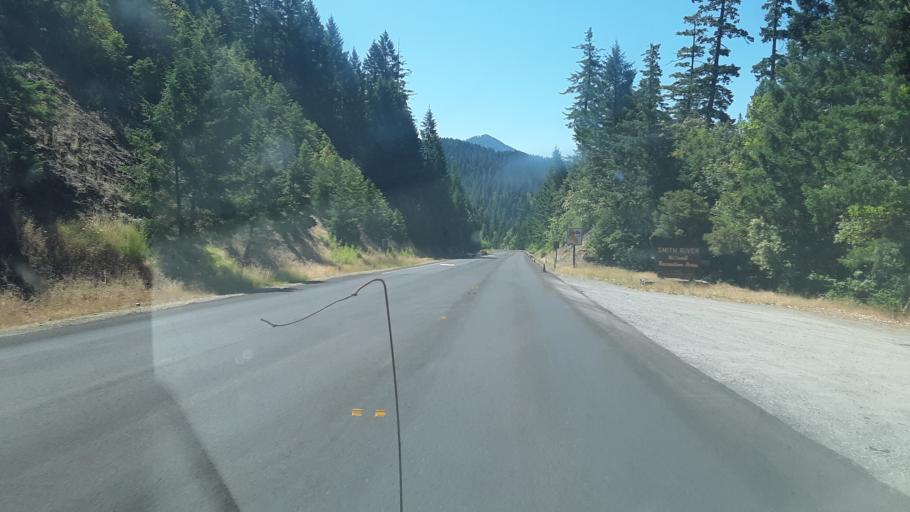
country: US
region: Oregon
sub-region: Josephine County
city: Cave Junction
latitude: 41.9641
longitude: -123.7468
